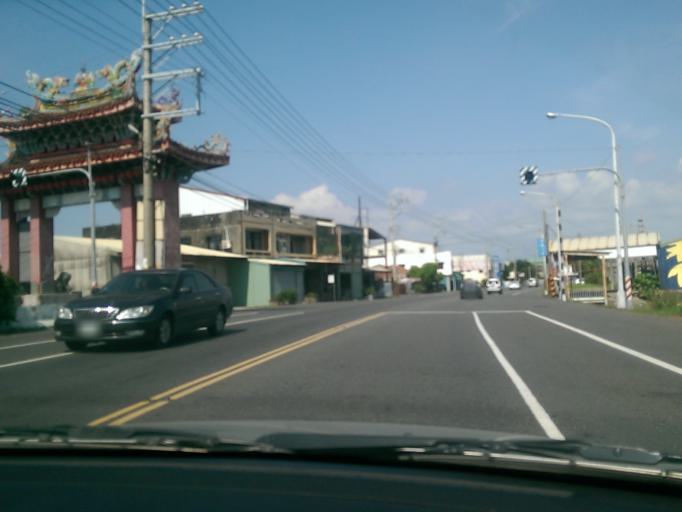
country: TW
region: Taiwan
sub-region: Chiayi
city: Taibao
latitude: 23.5612
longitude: 120.3110
